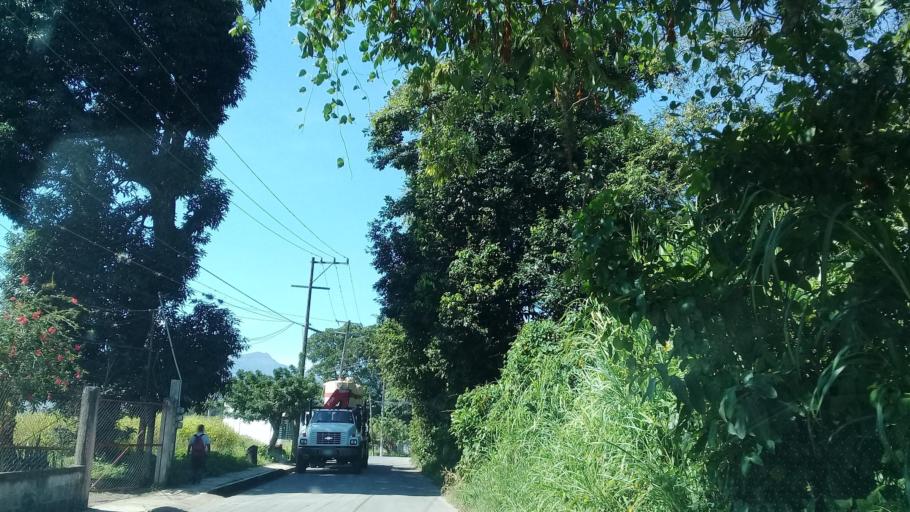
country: MX
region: Veracruz
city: Amatlan de los Reyes
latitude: 18.8540
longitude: -96.9115
